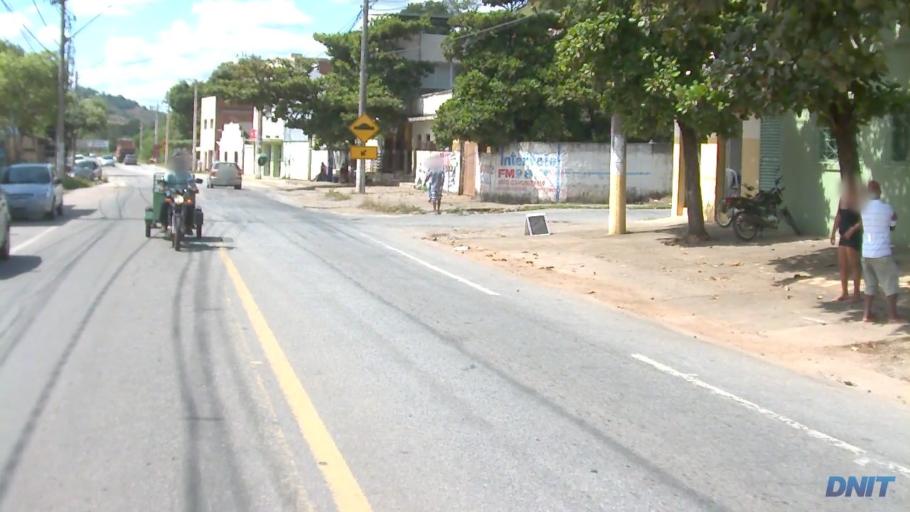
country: BR
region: Minas Gerais
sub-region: Coronel Fabriciano
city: Coronel Fabriciano
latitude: -19.5308
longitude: -42.6657
